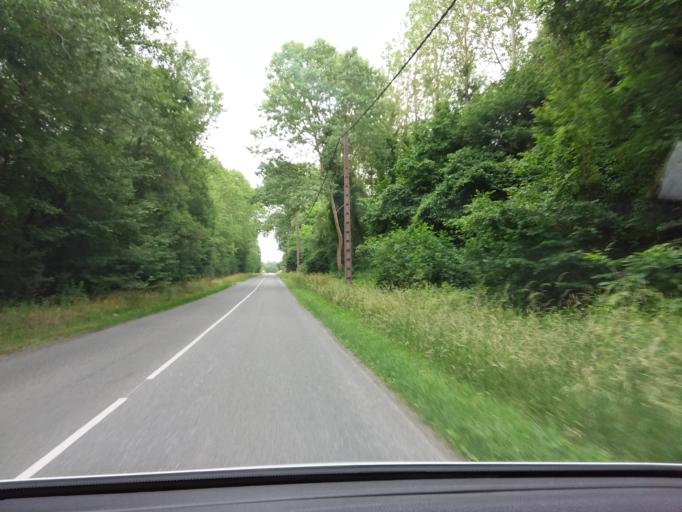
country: FR
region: Champagne-Ardenne
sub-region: Departement de la Marne
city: Fismes
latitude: 49.4006
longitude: 3.6272
